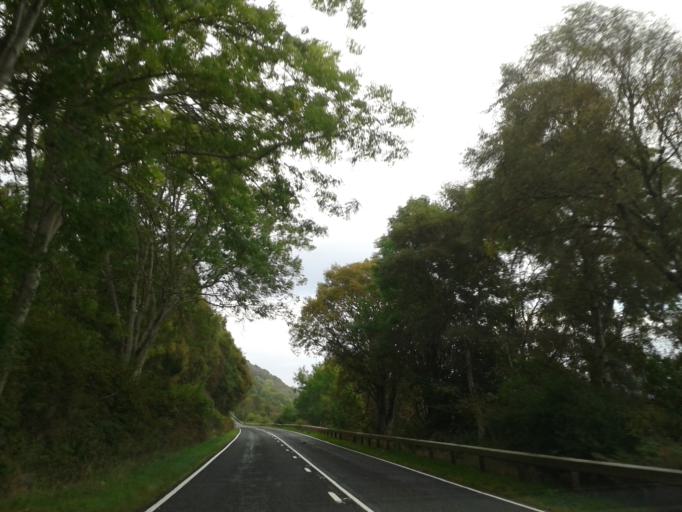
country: GB
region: Scotland
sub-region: Highland
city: Beauly
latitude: 57.3054
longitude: -4.4661
